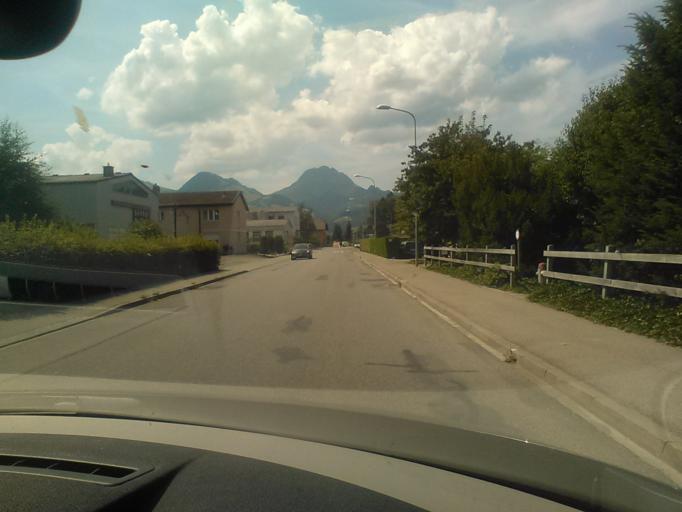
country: CH
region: Fribourg
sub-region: Gruyere District
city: Broc
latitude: 46.6068
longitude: 7.0988
